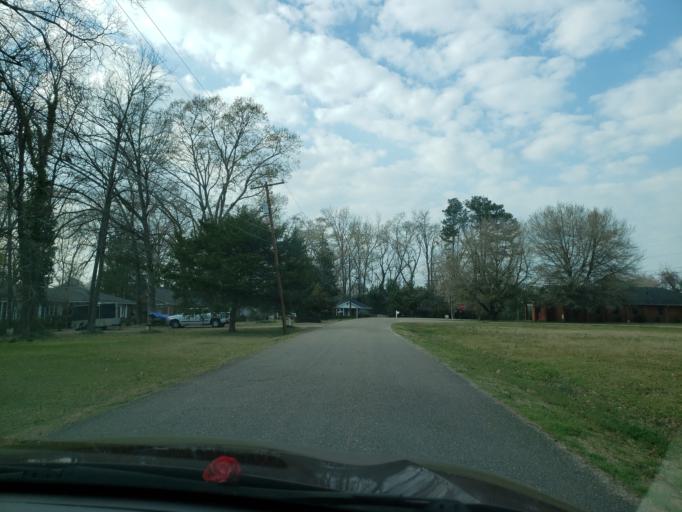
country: US
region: Alabama
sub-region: Hale County
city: Greensboro
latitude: 32.6975
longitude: -87.5954
